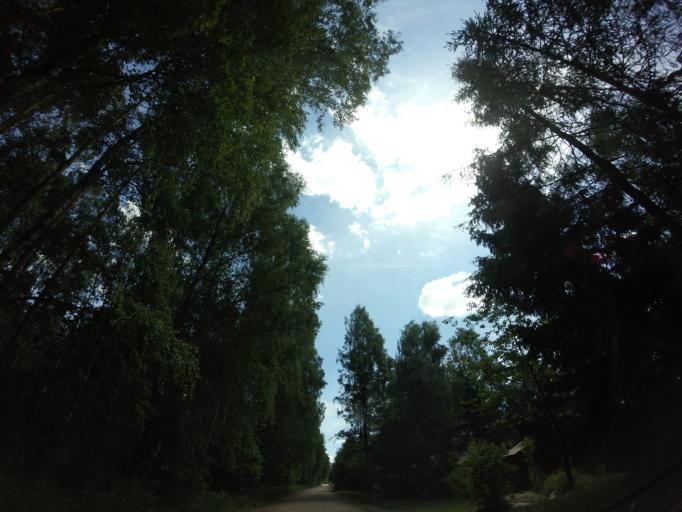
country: PL
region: West Pomeranian Voivodeship
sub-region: Powiat choszczenski
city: Drawno
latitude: 53.2134
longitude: 15.8325
